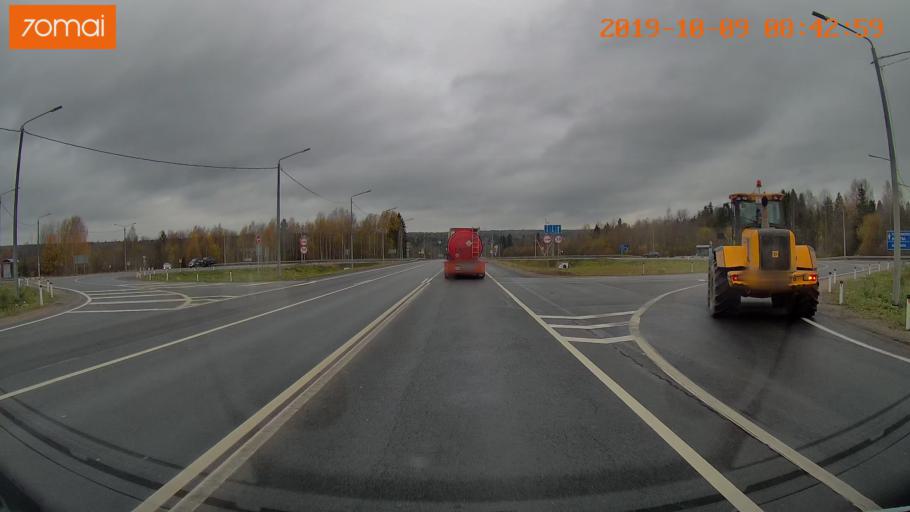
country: RU
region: Vologda
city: Gryazovets
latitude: 59.0201
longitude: 40.1163
